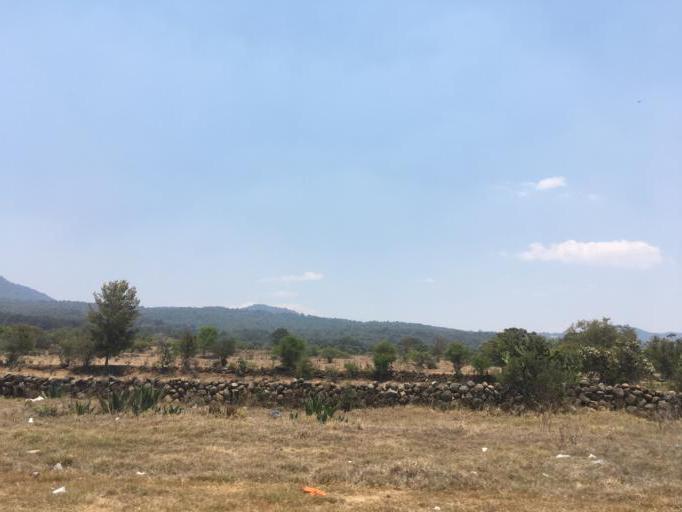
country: MX
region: Michoacan
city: Quiroga
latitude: 19.6508
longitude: -101.4929
